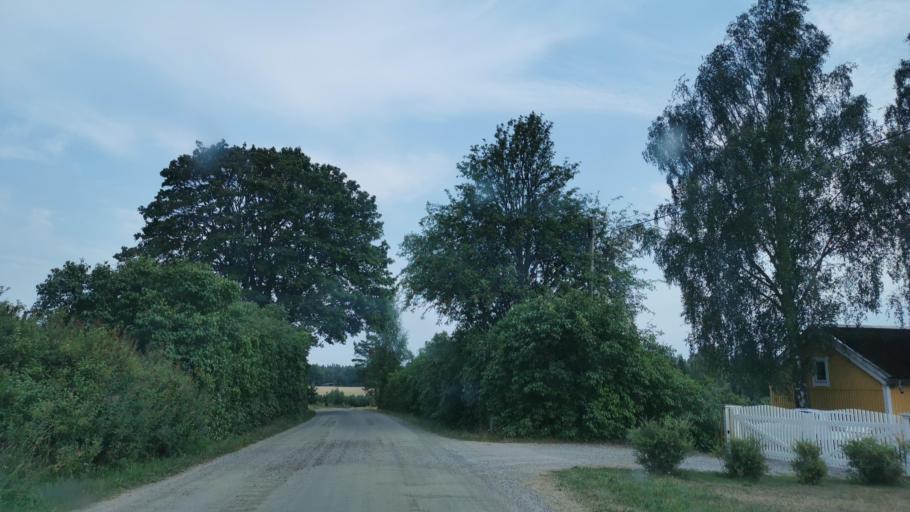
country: SE
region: OEstergoetland
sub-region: Norrkopings Kommun
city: Svartinge
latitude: 58.7239
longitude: 15.9492
